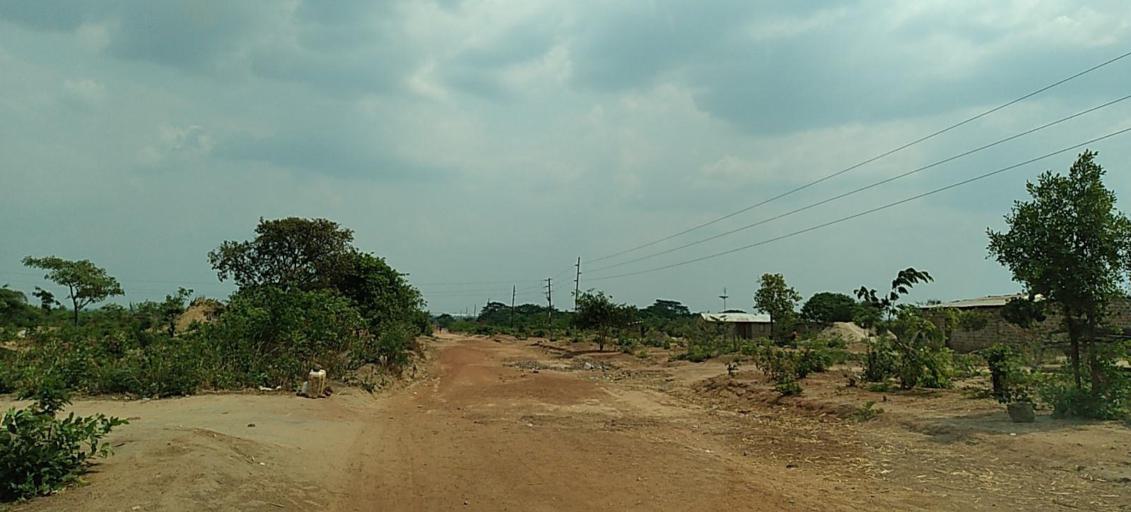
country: ZM
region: Copperbelt
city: Kalulushi
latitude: -12.8677
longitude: 28.0779
